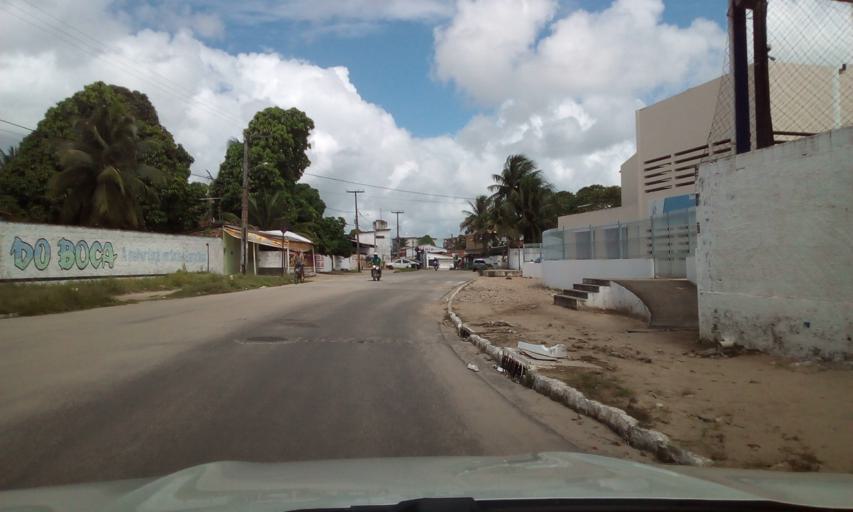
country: BR
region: Paraiba
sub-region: Joao Pessoa
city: Joao Pessoa
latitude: -7.1814
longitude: -34.8691
